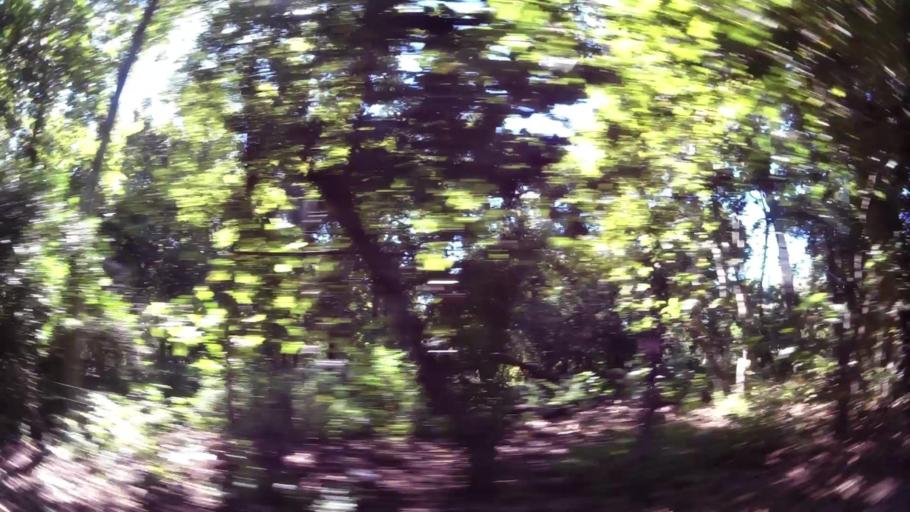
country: GT
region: Escuintla
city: Iztapa
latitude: 13.9232
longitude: -90.5946
